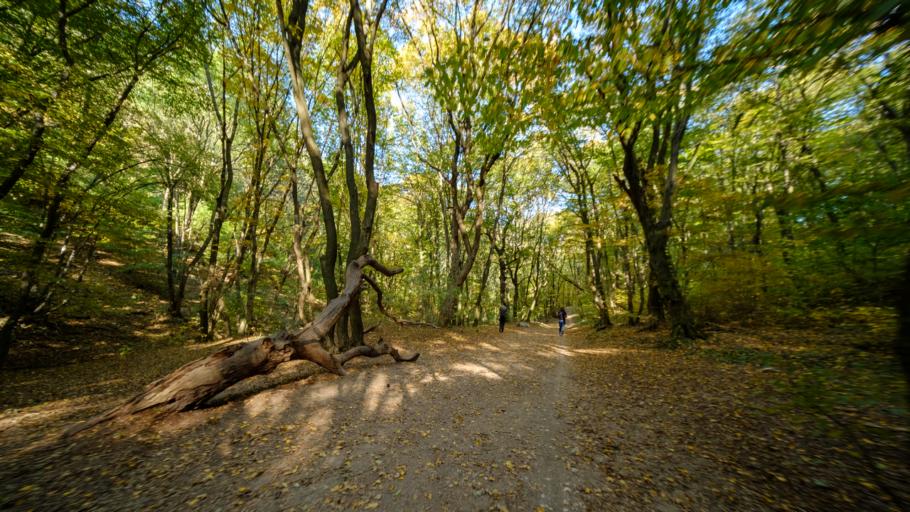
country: HU
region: Pest
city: Solymar
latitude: 47.5592
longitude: 18.9329
